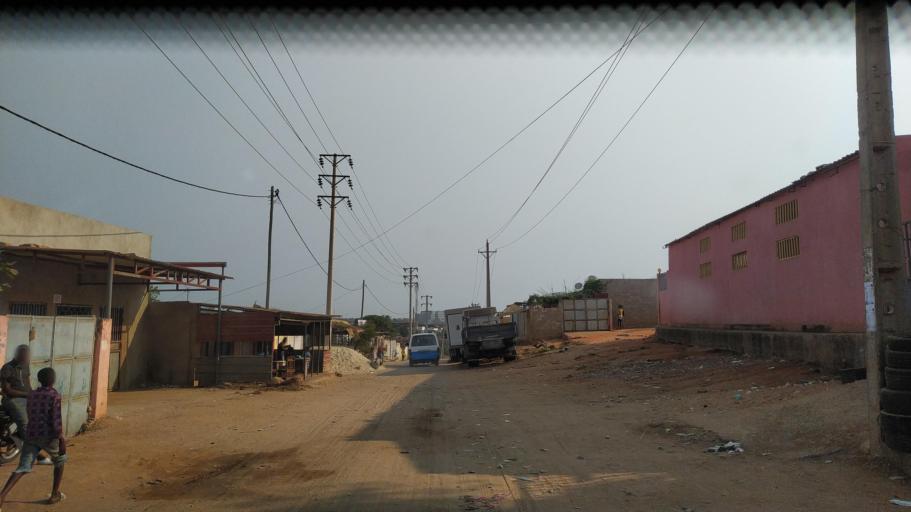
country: AO
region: Luanda
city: Luanda
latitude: -8.8693
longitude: 13.1996
